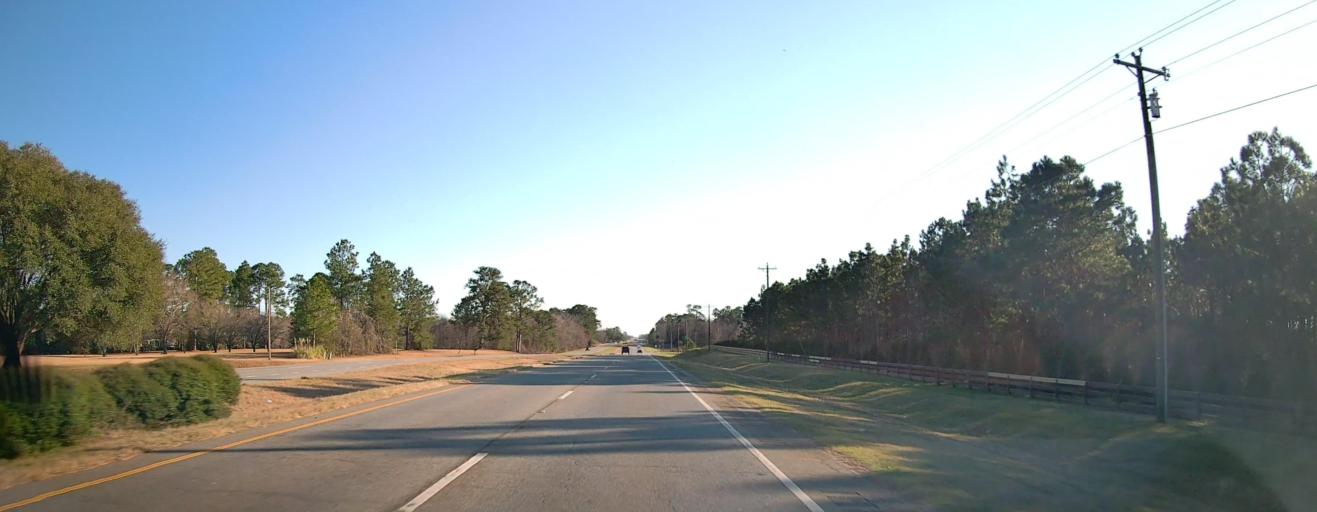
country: US
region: Georgia
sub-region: Lee County
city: Leesburg
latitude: 31.7101
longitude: -84.1726
